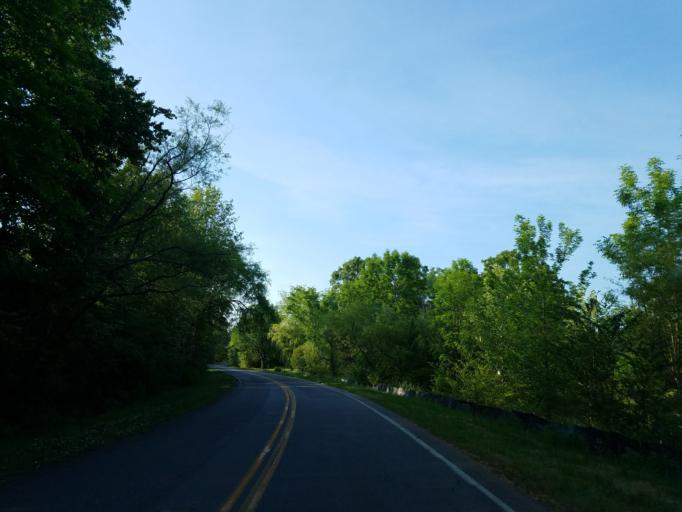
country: US
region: Georgia
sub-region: Floyd County
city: Shannon
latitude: 34.4758
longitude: -85.1373
